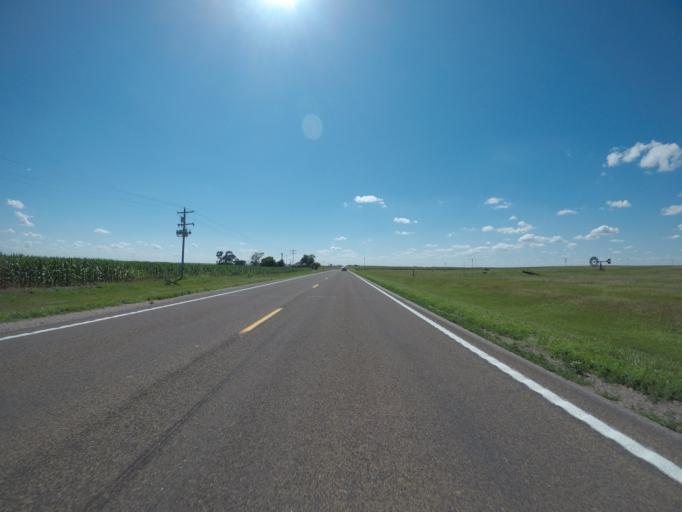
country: US
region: Nebraska
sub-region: Chase County
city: Imperial
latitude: 40.5376
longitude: -101.8160
